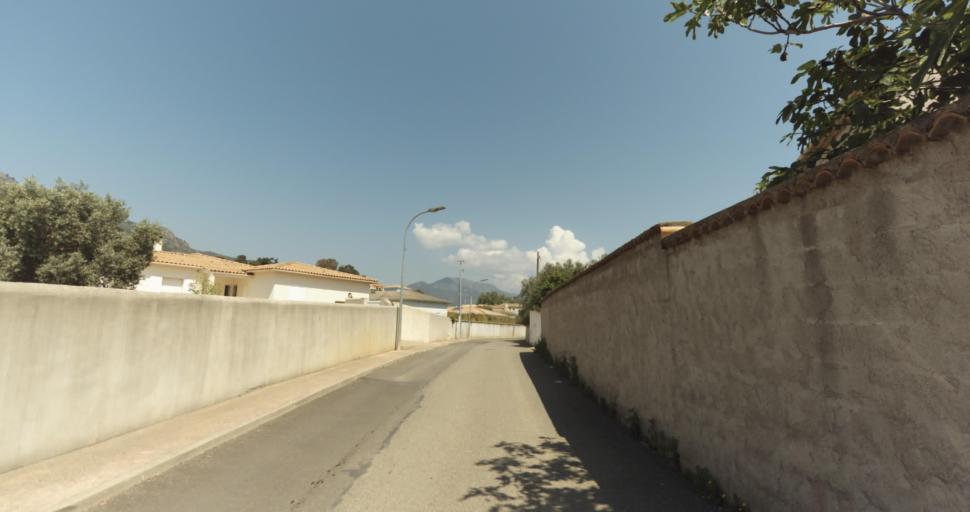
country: FR
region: Corsica
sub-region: Departement de la Haute-Corse
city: Biguglia
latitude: 42.6166
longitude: 9.4347
